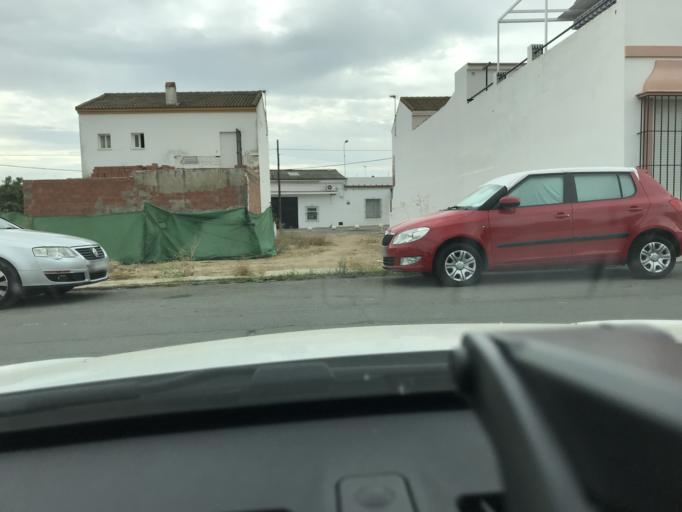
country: ES
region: Andalusia
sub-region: Provincia de Sevilla
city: Villanueva del Rio y Minas
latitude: 37.6496
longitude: -5.7110
